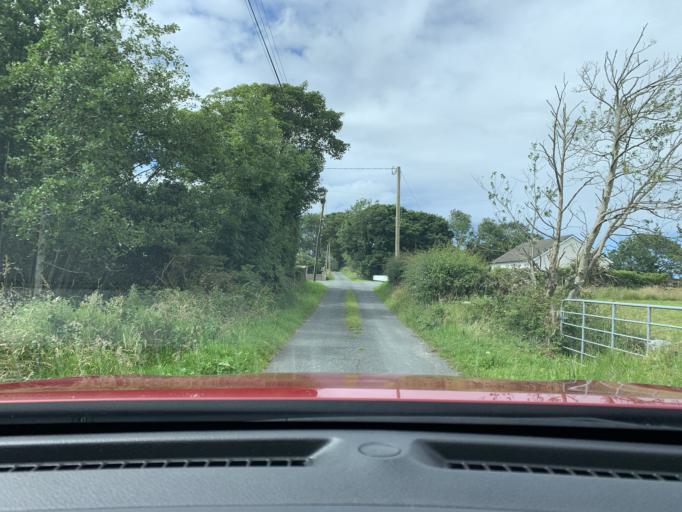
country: IE
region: Connaught
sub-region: Sligo
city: Sligo
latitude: 54.3816
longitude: -8.5169
